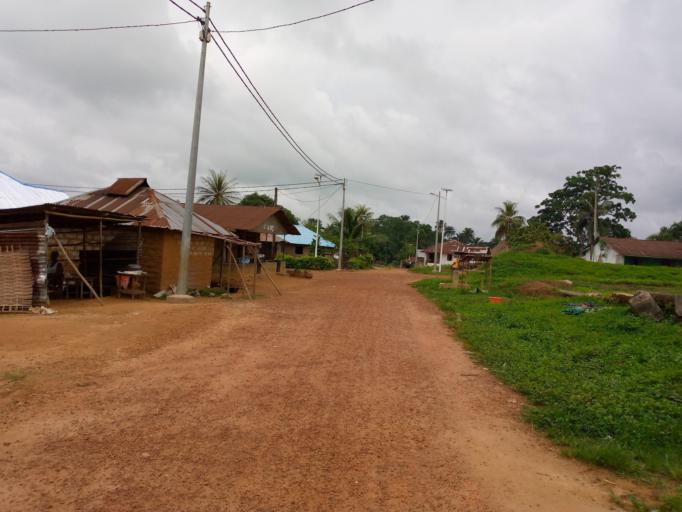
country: SL
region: Southern Province
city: Sumbuya
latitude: 7.5627
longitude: -12.0889
